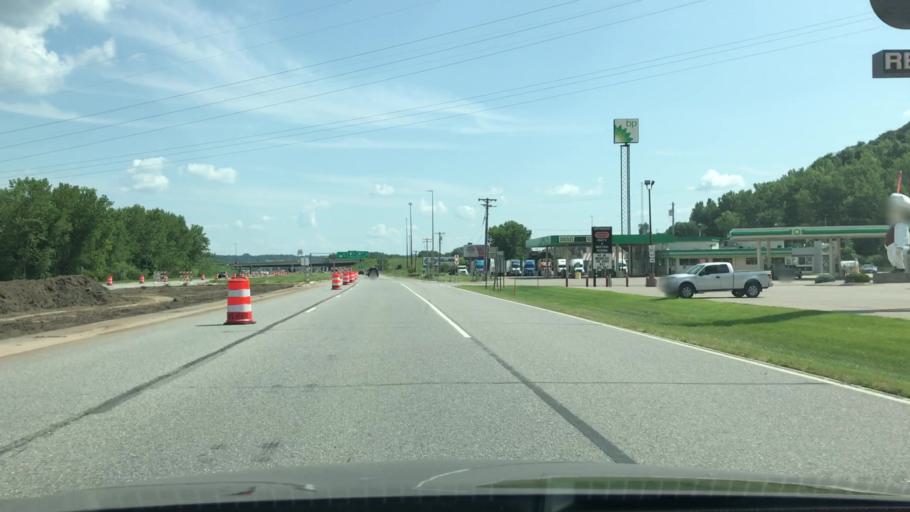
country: US
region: Minnesota
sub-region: Nicollet County
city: North Mankato
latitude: 44.1970
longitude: -94.0205
